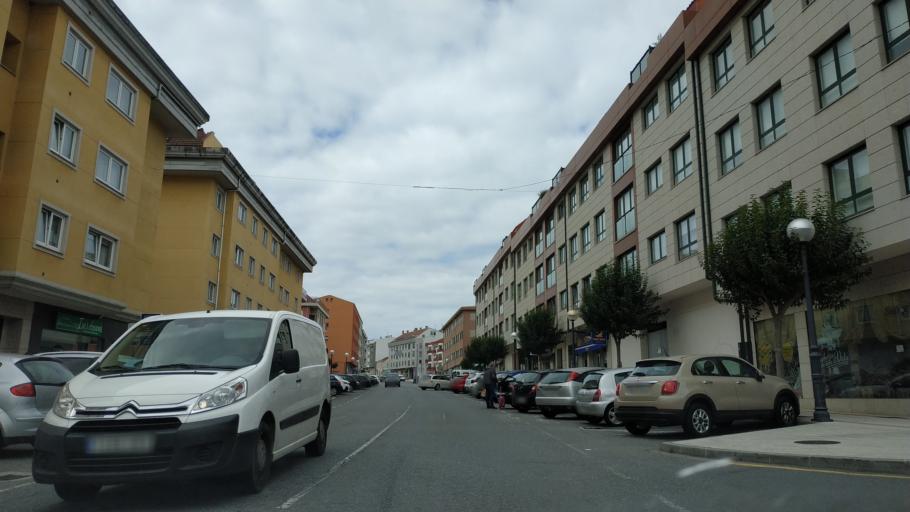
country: ES
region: Galicia
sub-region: Provincia da Coruna
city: Arteixo
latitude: 43.3027
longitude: -8.5131
